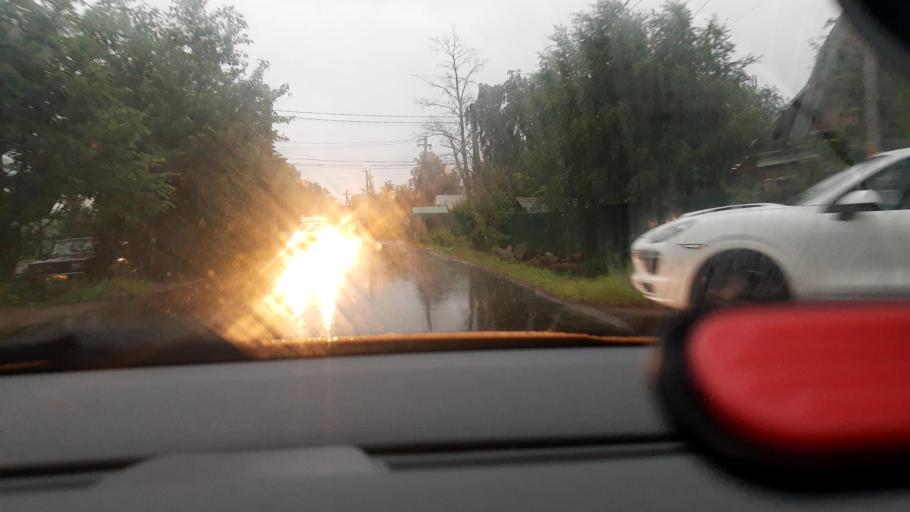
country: RU
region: Moskovskaya
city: Alabushevo
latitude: 56.0084
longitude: 37.1312
